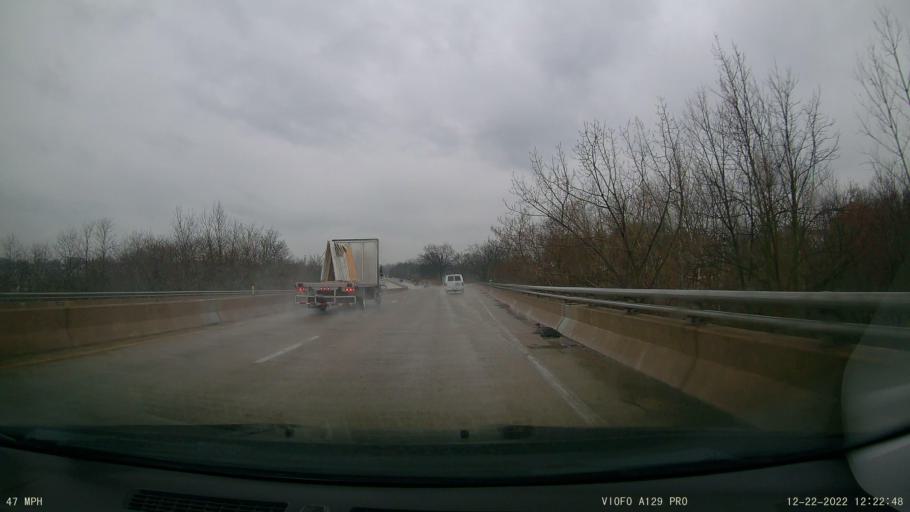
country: US
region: Pennsylvania
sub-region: Montgomery County
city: Bridgeport
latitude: 40.1096
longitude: -75.3527
